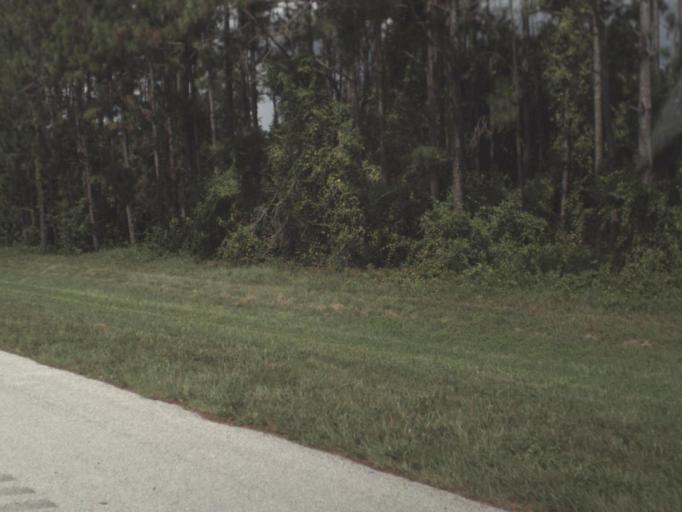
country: US
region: Florida
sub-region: Hillsborough County
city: Ruskin
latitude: 27.6539
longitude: -82.4403
